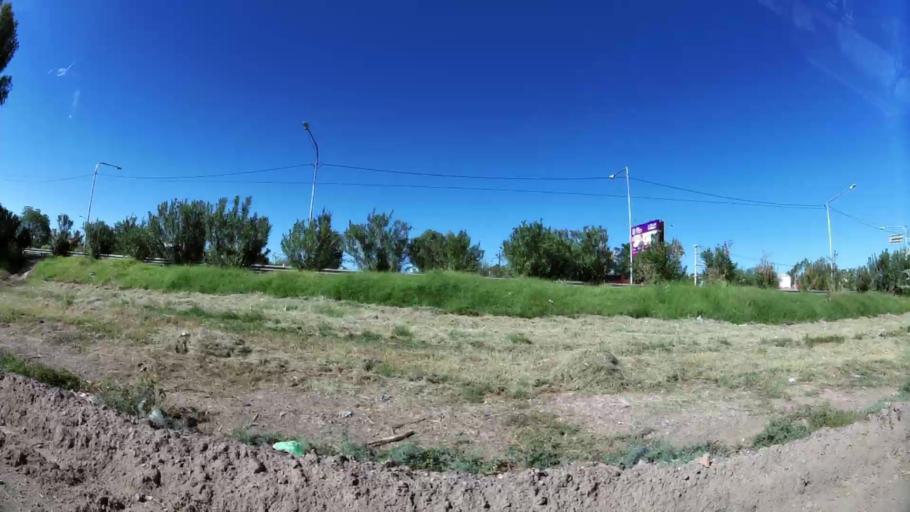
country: AR
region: Mendoza
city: Las Heras
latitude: -32.8375
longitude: -68.8052
